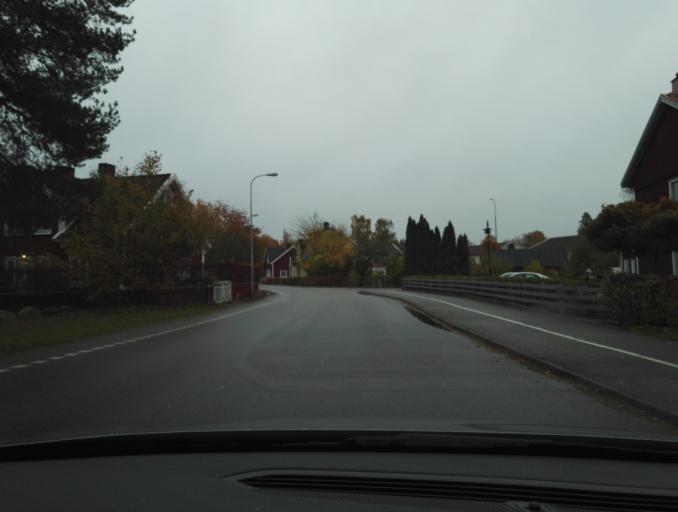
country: SE
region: Kronoberg
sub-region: Vaxjo Kommun
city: Rottne
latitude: 57.0217
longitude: 14.8936
